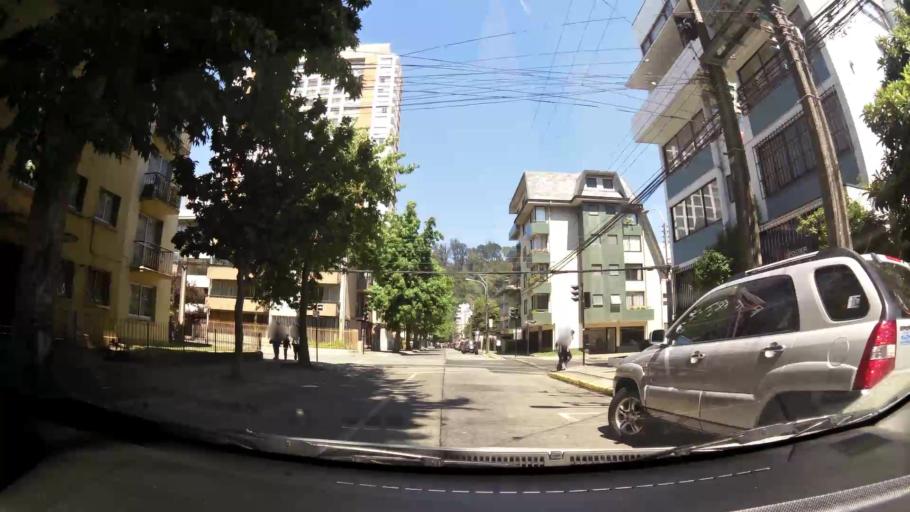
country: CL
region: Biobio
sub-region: Provincia de Concepcion
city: Concepcion
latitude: -36.8281
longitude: -73.0455
